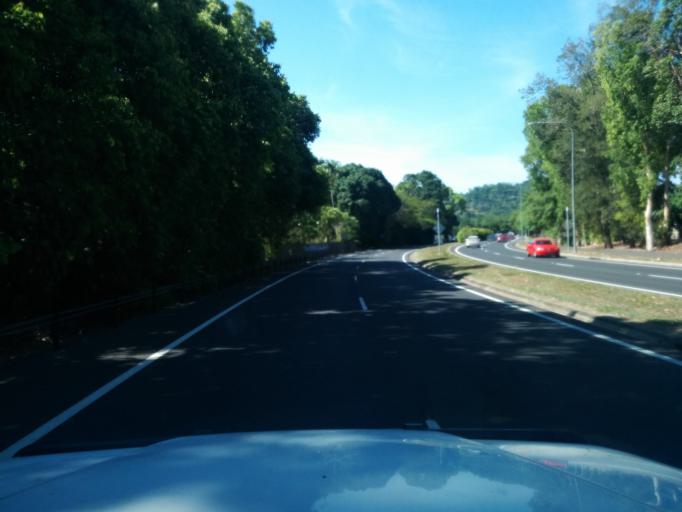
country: AU
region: Queensland
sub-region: Cairns
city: Redlynch
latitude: -16.9030
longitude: 145.7088
